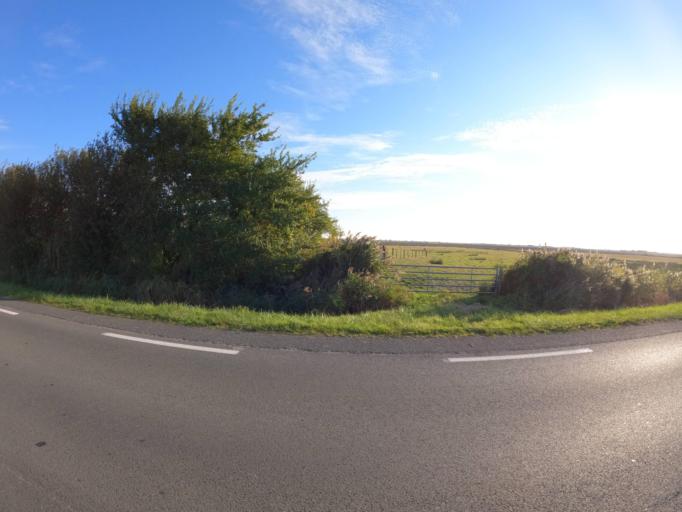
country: FR
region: Pays de la Loire
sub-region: Departement de la Vendee
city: Chaille-les-Marais
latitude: 46.4129
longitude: -1.0522
